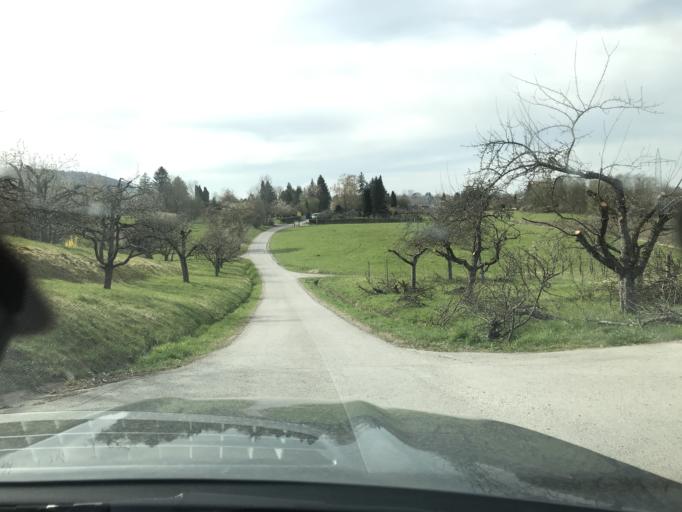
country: DE
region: Baden-Wuerttemberg
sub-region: Regierungsbezirk Stuttgart
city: Waiblingen
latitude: 48.7944
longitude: 9.3245
